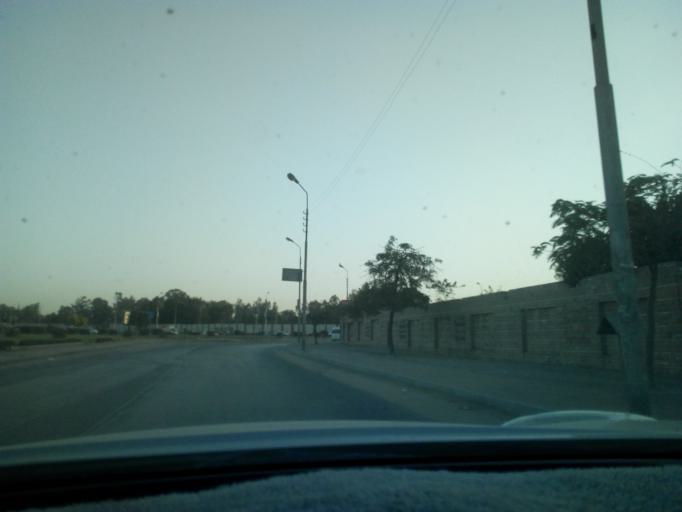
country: EG
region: Muhafazat al Qalyubiyah
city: Al Khankah
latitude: 30.1183
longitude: 31.3639
